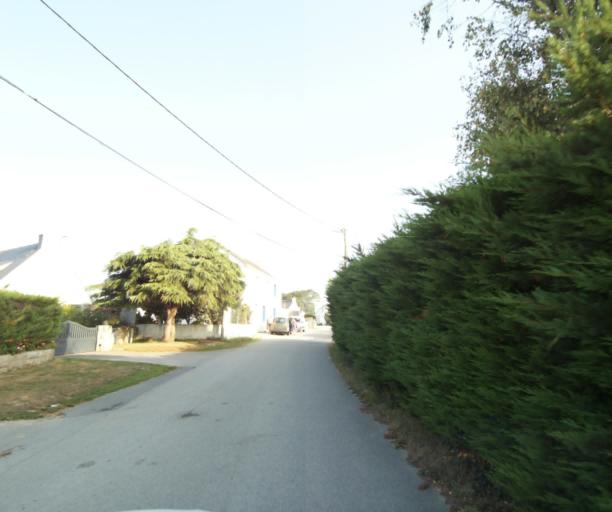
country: FR
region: Brittany
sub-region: Departement du Morbihan
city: Riantec
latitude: 47.7049
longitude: -3.2991
